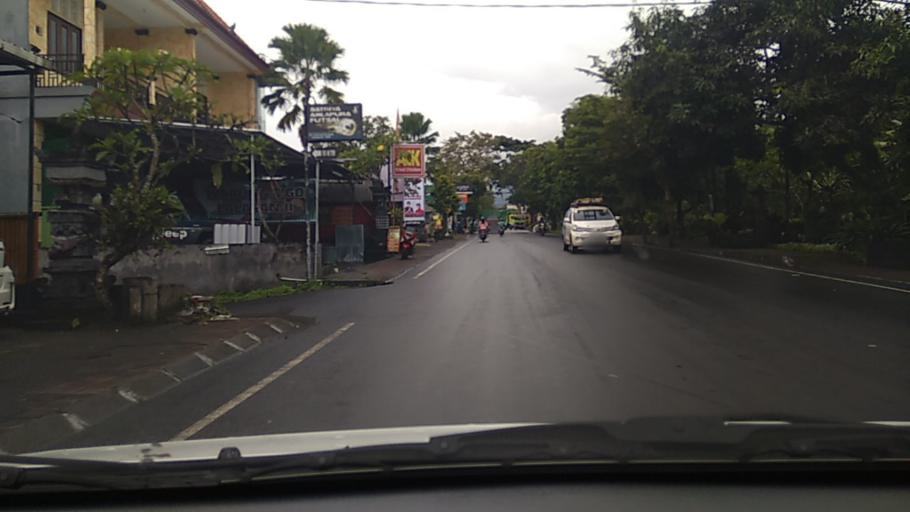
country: ID
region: Bali
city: Subagan
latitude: -8.4406
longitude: 115.5973
